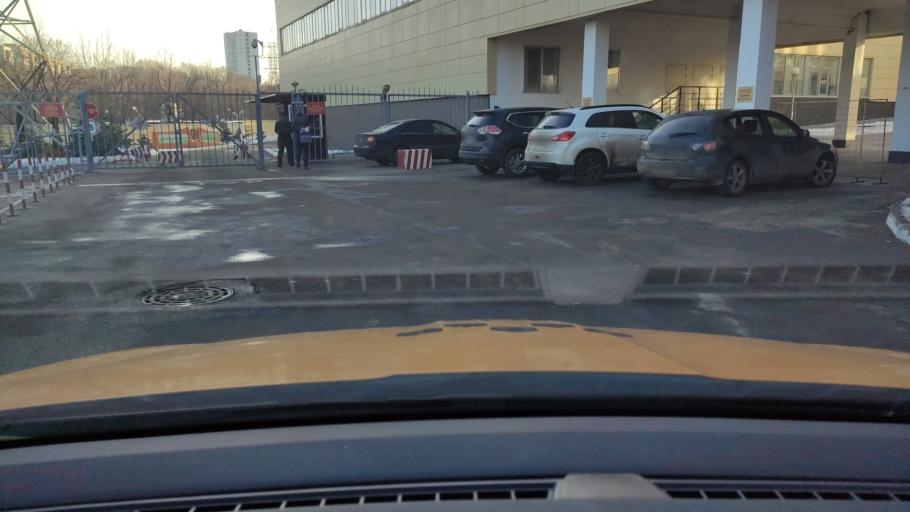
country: RU
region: Moskovskaya
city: Kozhukhovo
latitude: 55.6748
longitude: 37.6505
